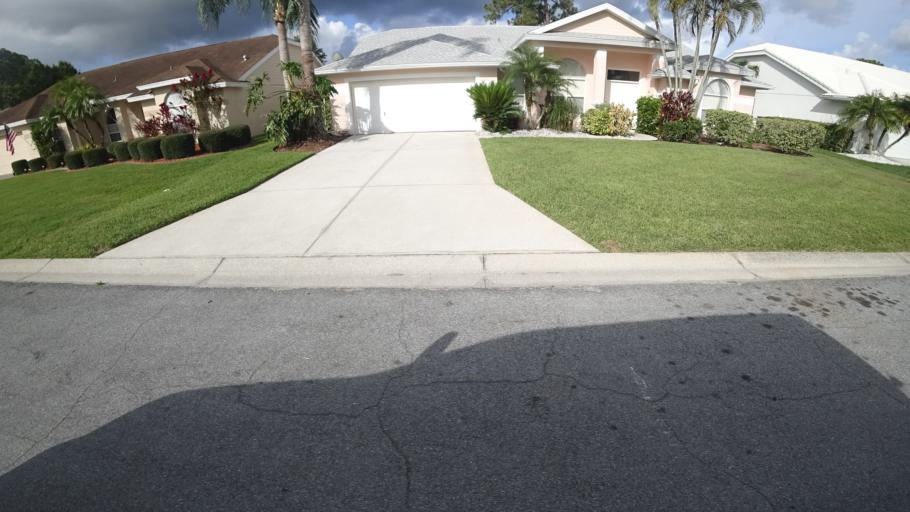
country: US
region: Florida
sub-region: Sarasota County
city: Desoto Lakes
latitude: 27.4163
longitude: -82.4822
